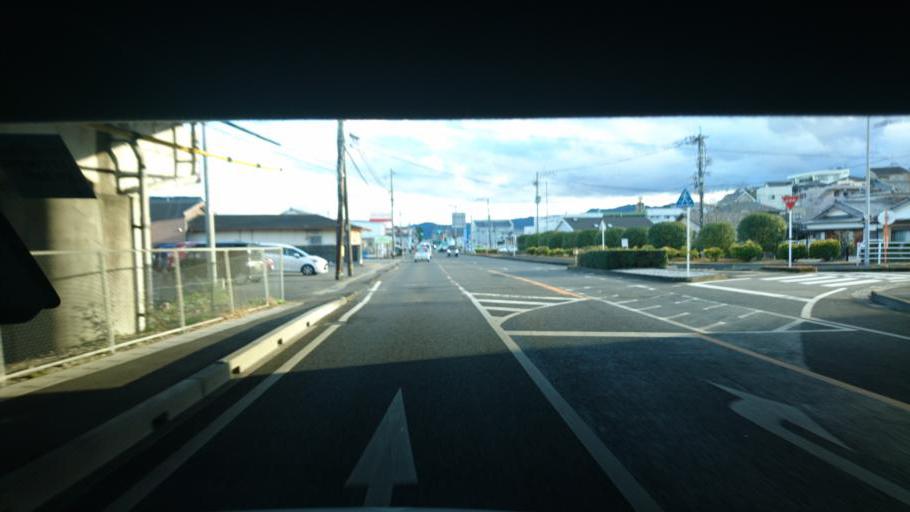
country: JP
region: Miyazaki
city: Miyazaki-shi
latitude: 31.8673
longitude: 131.4318
